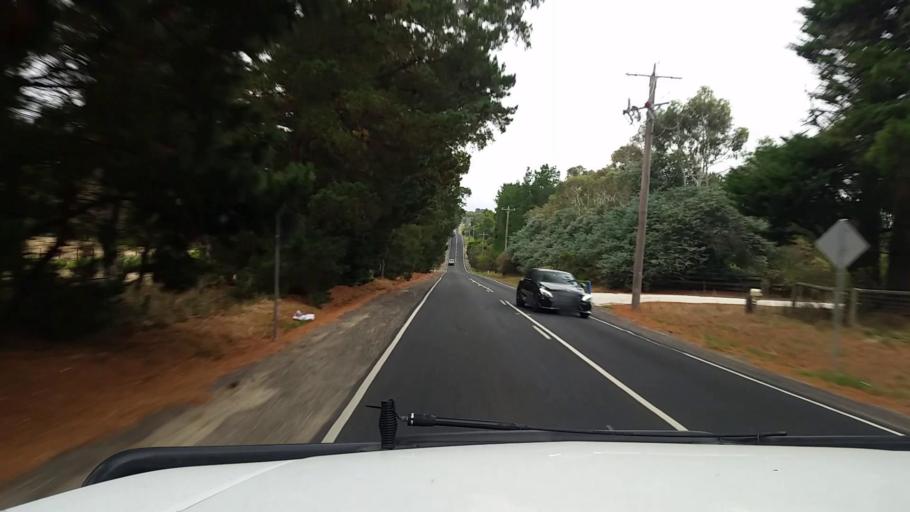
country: AU
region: Victoria
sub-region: Mornington Peninsula
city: Hastings
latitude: -38.2977
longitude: 145.1457
